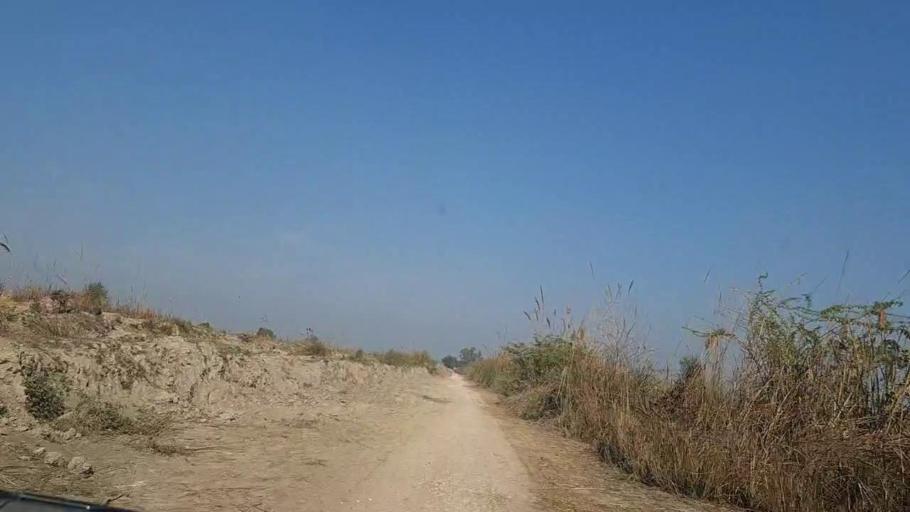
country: PK
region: Sindh
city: Sakrand
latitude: 26.0882
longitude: 68.3670
